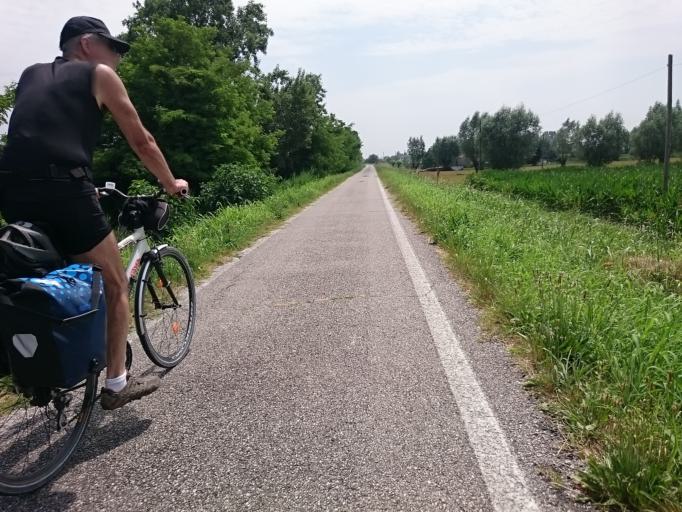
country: IT
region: Veneto
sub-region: Provincia di Venezia
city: Valli
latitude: 45.2025
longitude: 12.1849
